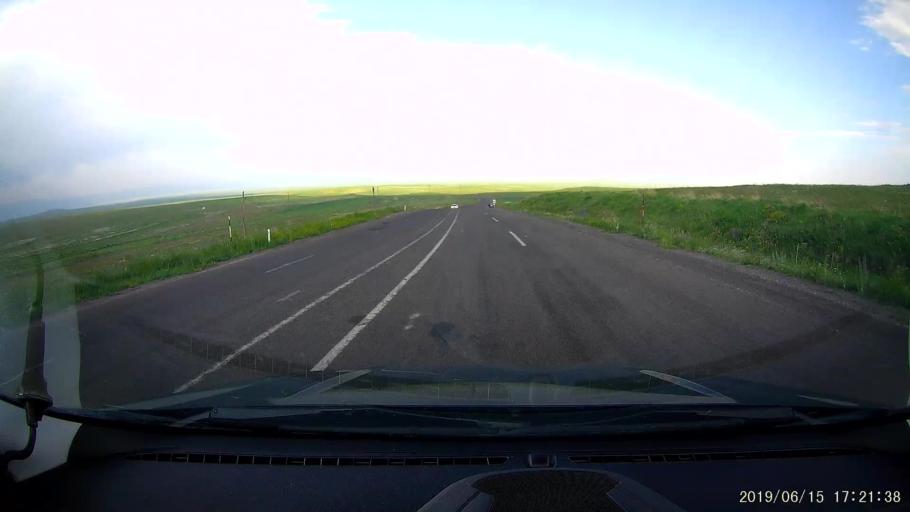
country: TR
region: Kars
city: Basgedikler
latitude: 40.6169
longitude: 43.3278
